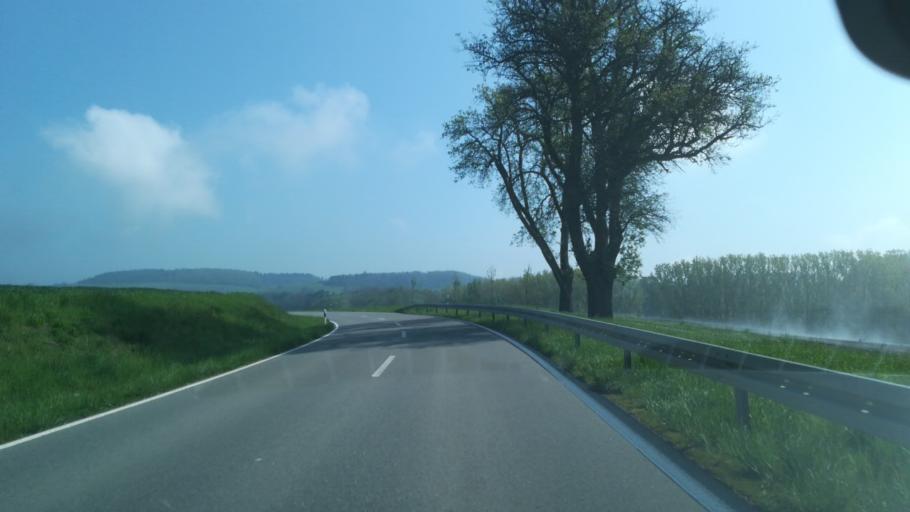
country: DE
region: Baden-Wuerttemberg
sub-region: Freiburg Region
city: Hilzingen
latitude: 47.7718
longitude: 8.7889
